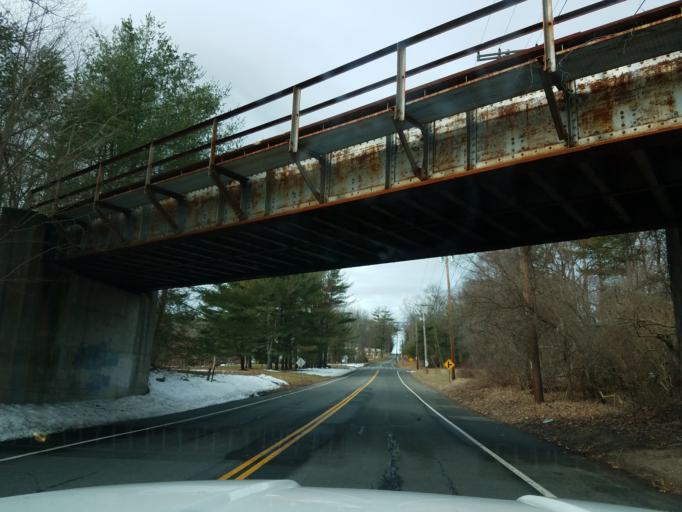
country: US
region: Connecticut
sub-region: Hartford County
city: Weatogue
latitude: 41.8039
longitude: -72.8336
